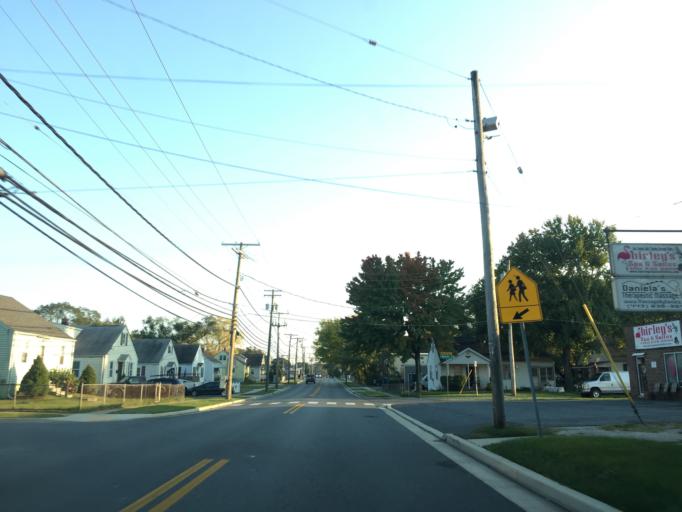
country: US
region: Maryland
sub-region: Baltimore County
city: Essex
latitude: 39.3055
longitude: -76.4635
